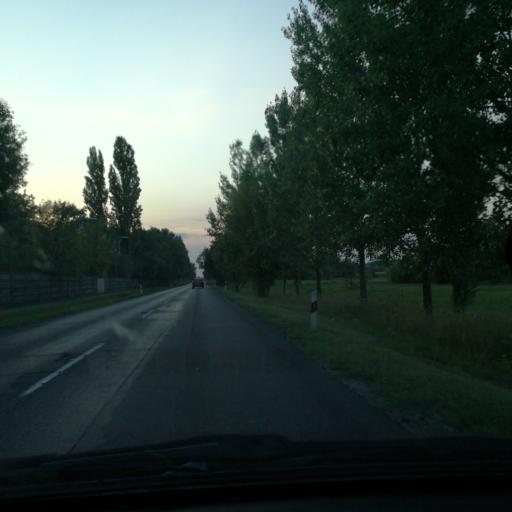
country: HU
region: Bacs-Kiskun
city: Kiskoros
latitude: 46.6061
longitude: 19.3094
